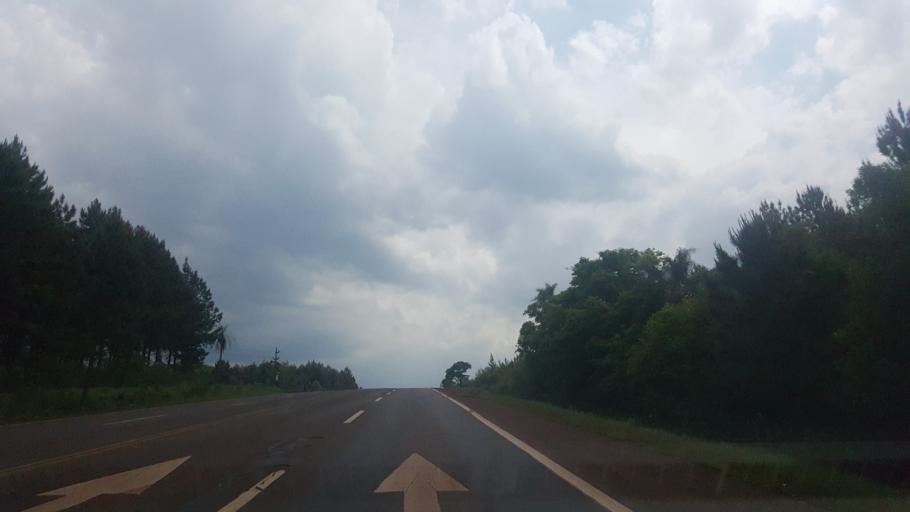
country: AR
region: Misiones
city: Santo Pipo
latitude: -27.1056
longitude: -55.3255
